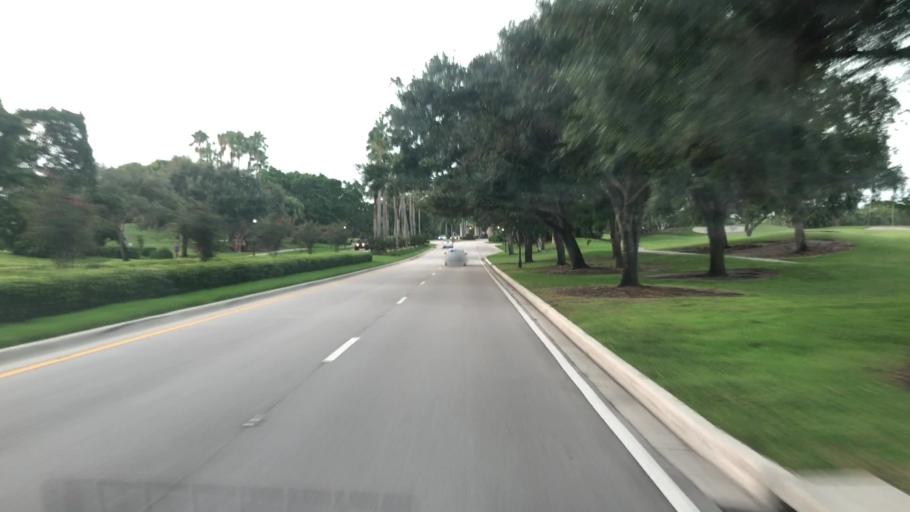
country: US
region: Florida
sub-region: Broward County
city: Weston
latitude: 26.0892
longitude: -80.3921
